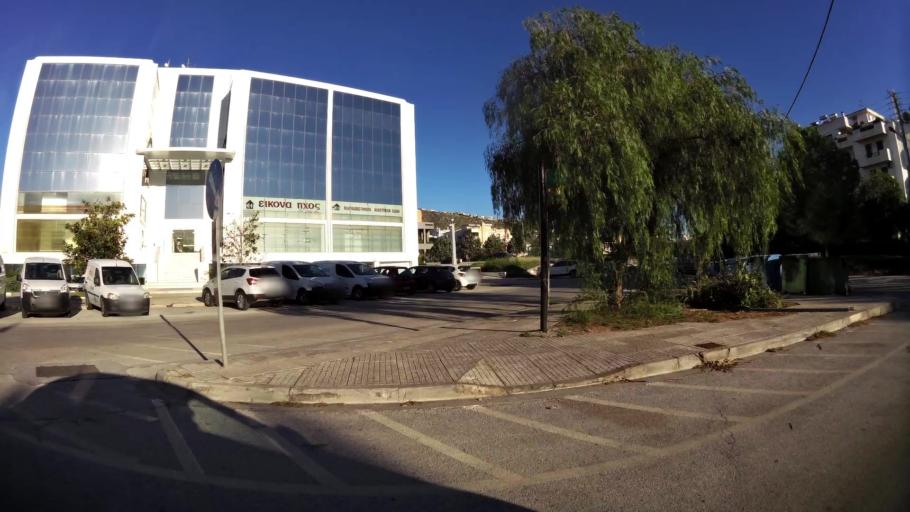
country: GR
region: Attica
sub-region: Nomarchia Athinas
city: Glyfada
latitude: 37.8635
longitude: 23.7609
